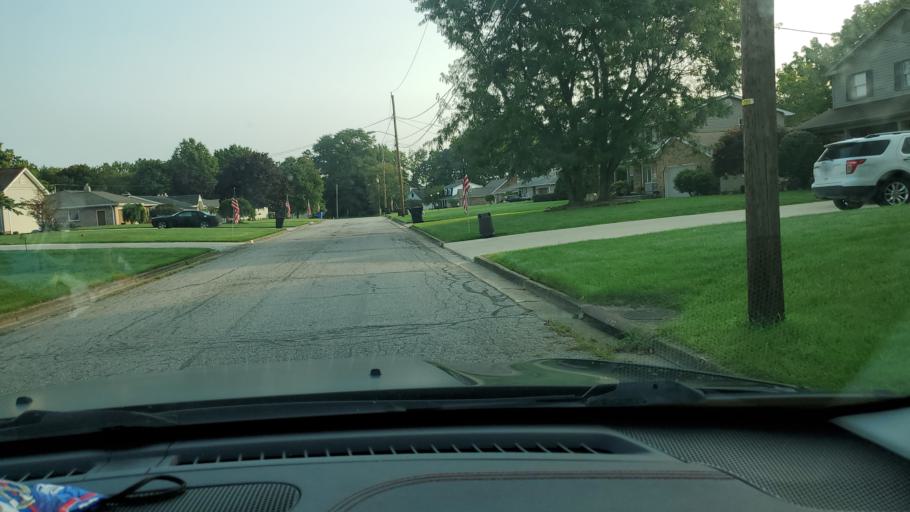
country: US
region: Ohio
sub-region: Mahoning County
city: Poland
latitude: 41.0331
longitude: -80.6018
